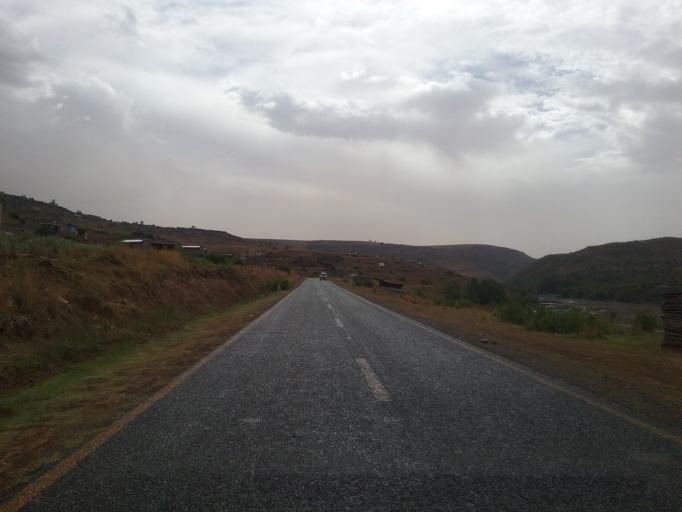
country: LS
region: Quthing
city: Quthing
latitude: -30.3667
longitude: 27.7195
